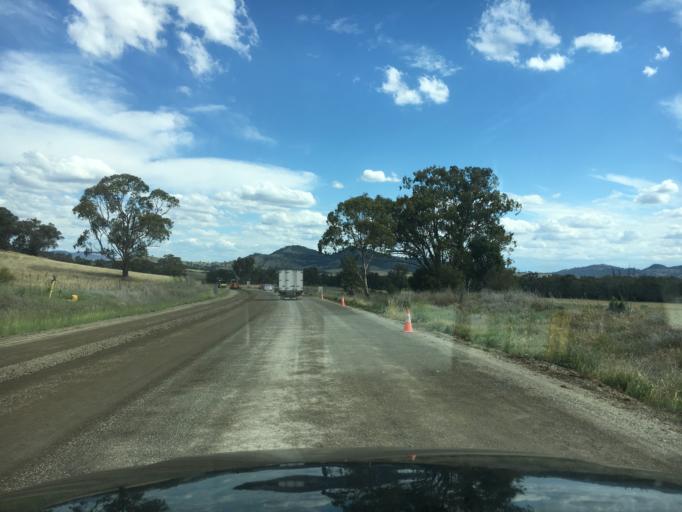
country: AU
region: New South Wales
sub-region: Liverpool Plains
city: Quirindi
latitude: -31.4542
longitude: 150.8611
